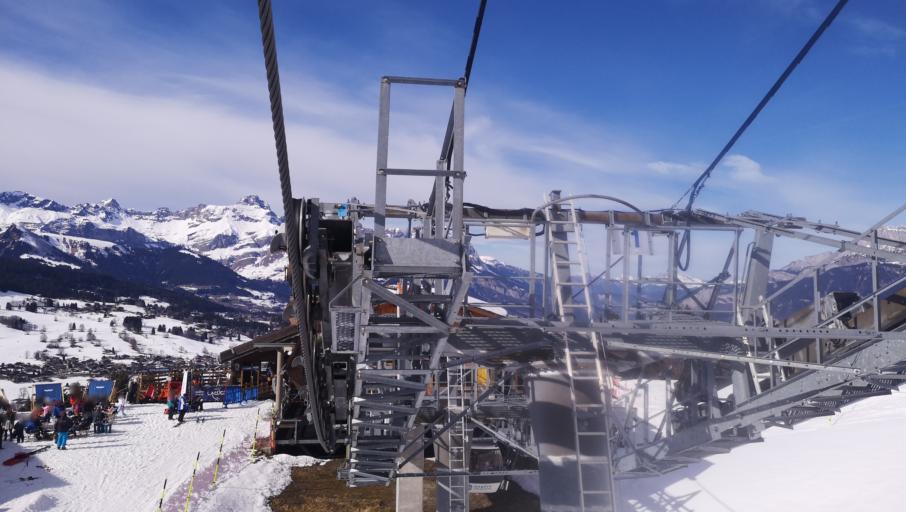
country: FR
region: Rhone-Alpes
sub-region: Departement de la Haute-Savoie
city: Combloux
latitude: 45.8720
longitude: 6.6512
